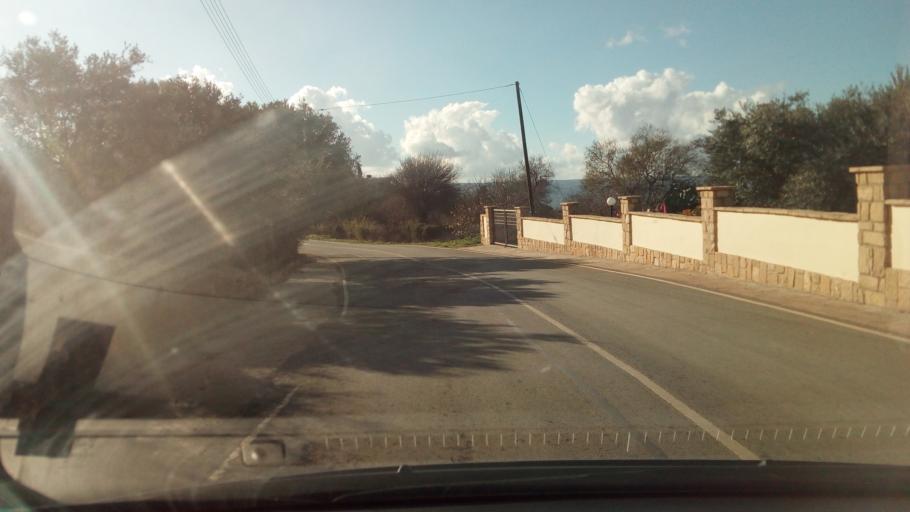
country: CY
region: Pafos
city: Tala
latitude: 34.9259
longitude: 32.5323
